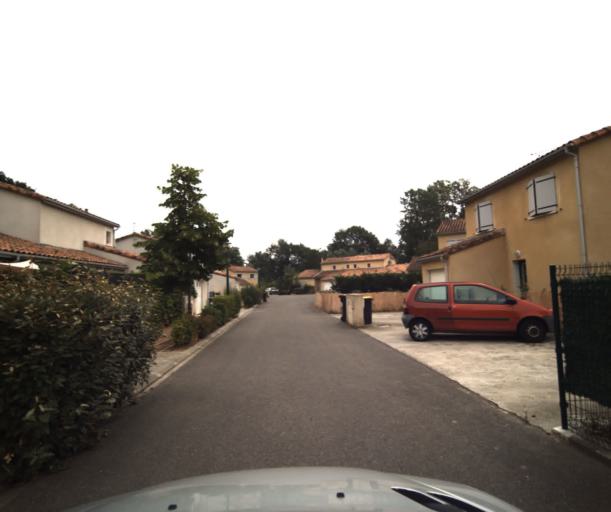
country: FR
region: Midi-Pyrenees
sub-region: Departement de la Haute-Garonne
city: Portet-sur-Garonne
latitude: 43.5385
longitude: 1.4154
